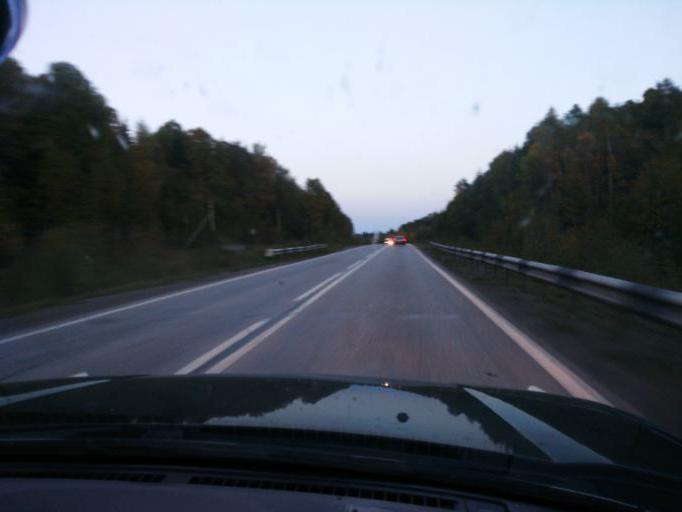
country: RU
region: Perm
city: Verkhnechusovskiye Gorodki
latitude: 58.2663
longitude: 56.9605
